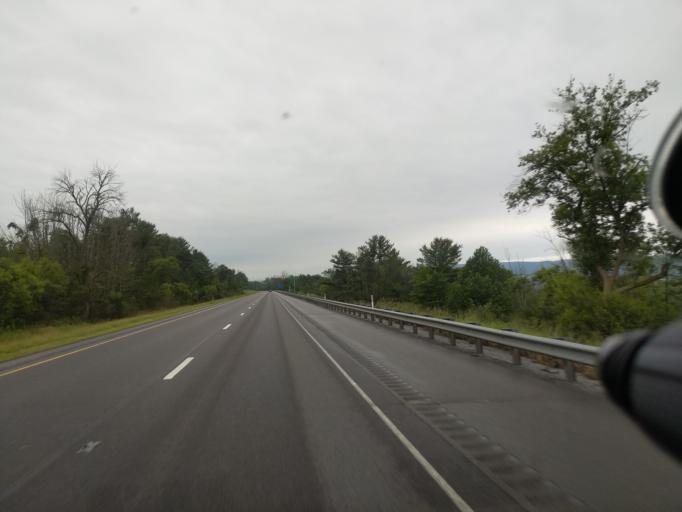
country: US
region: Pennsylvania
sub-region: Clinton County
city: Castanea
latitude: 41.0672
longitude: -77.4176
